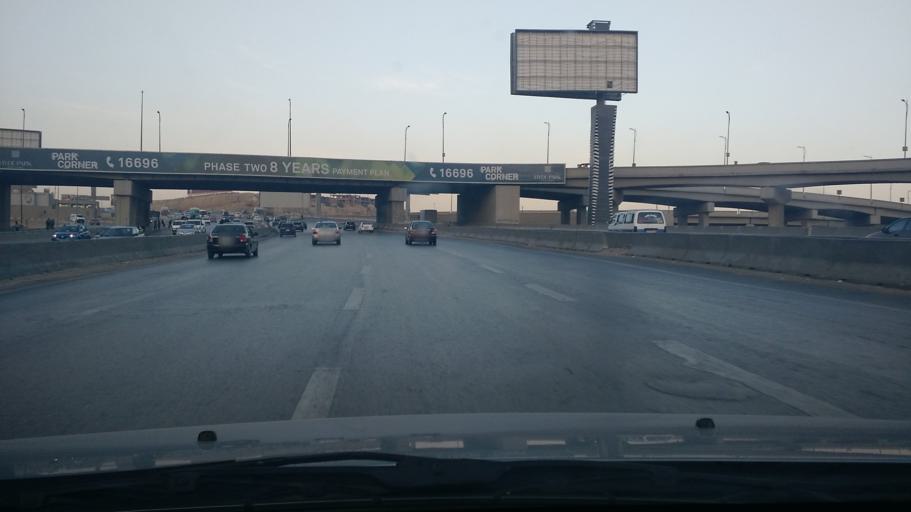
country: EG
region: Al Jizah
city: Al Hawamidiyah
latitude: 29.9784
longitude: 31.3582
